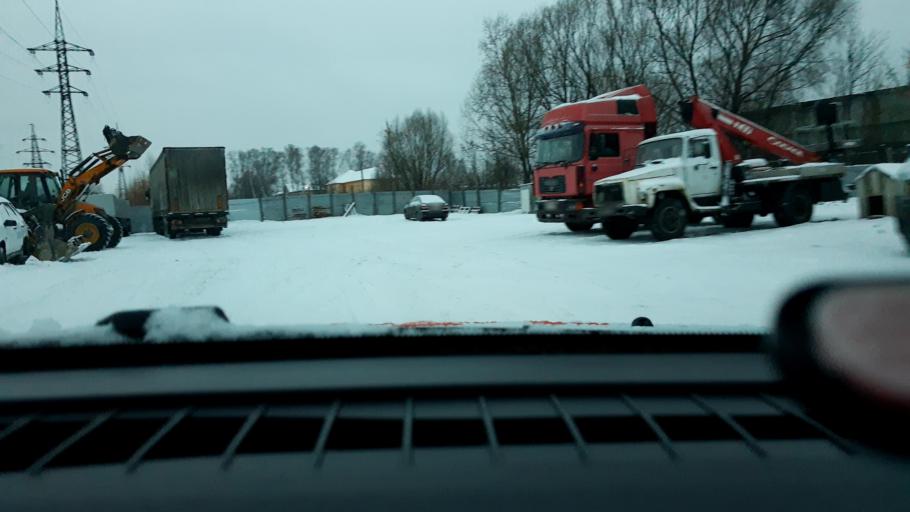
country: RU
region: Nizjnij Novgorod
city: Nizhniy Novgorod
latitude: 56.3100
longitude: 43.8796
